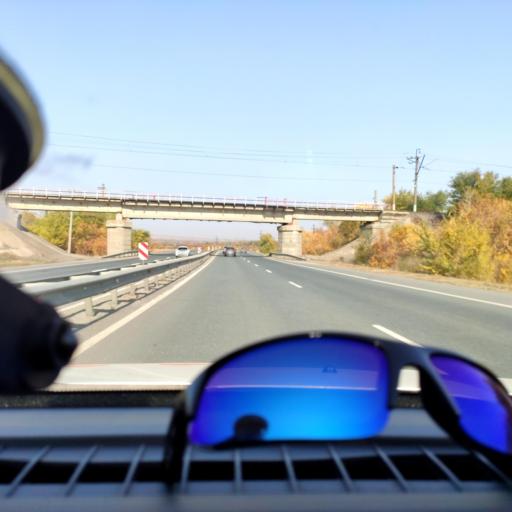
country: RU
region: Samara
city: Novokuybyshevsk
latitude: 53.0193
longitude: 49.9830
